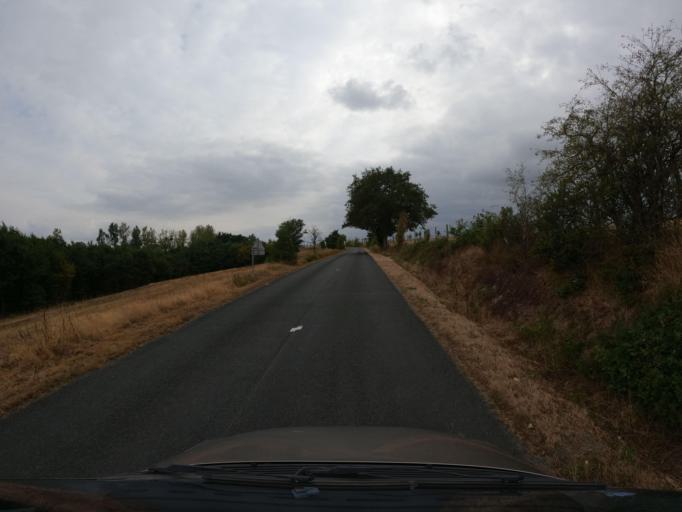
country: FR
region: Pays de la Loire
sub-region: Departement de la Vendee
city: Tiffauges
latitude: 46.9915
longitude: -1.1087
